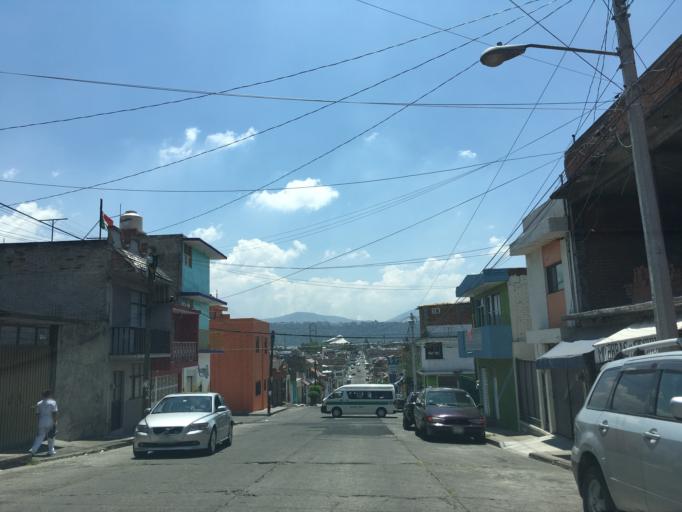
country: MX
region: Michoacan
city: Morelia
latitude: 19.7063
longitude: -101.1734
